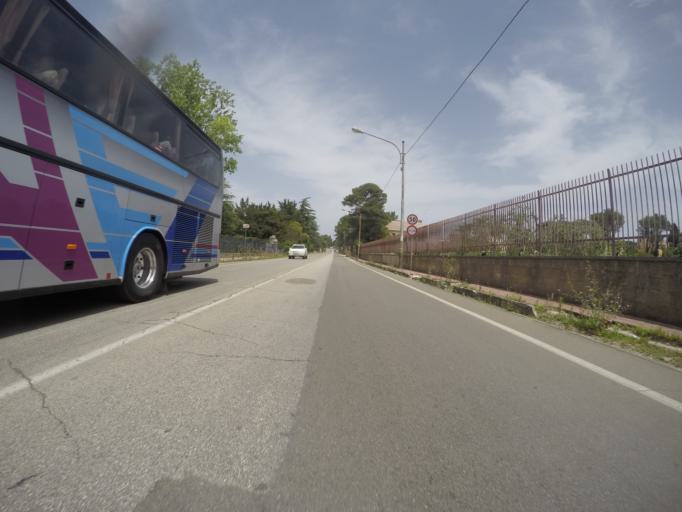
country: IT
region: Apulia
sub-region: Provincia di Taranto
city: Martina Franca
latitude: 40.6899
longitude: 17.3342
